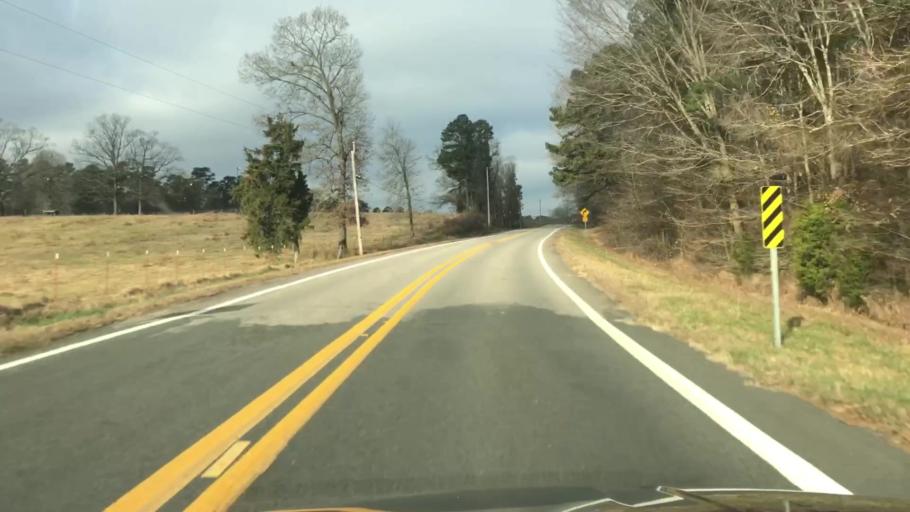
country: US
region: Arkansas
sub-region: Montgomery County
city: Mount Ida
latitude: 34.6599
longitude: -93.7661
